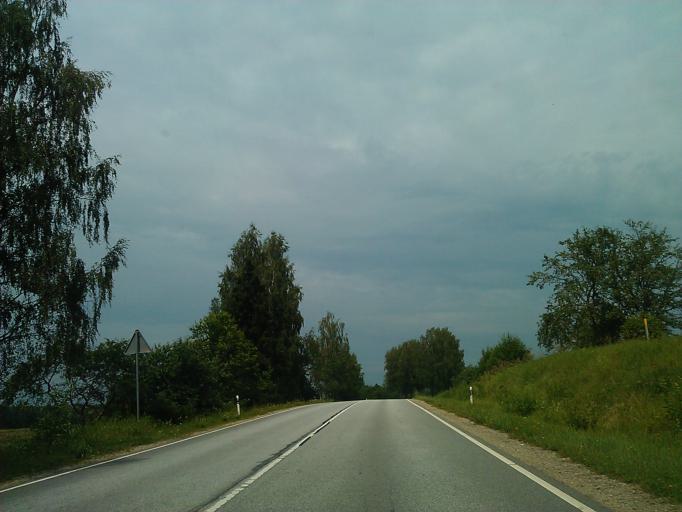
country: LV
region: Beverina
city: Murmuiza
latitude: 57.4515
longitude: 25.4262
